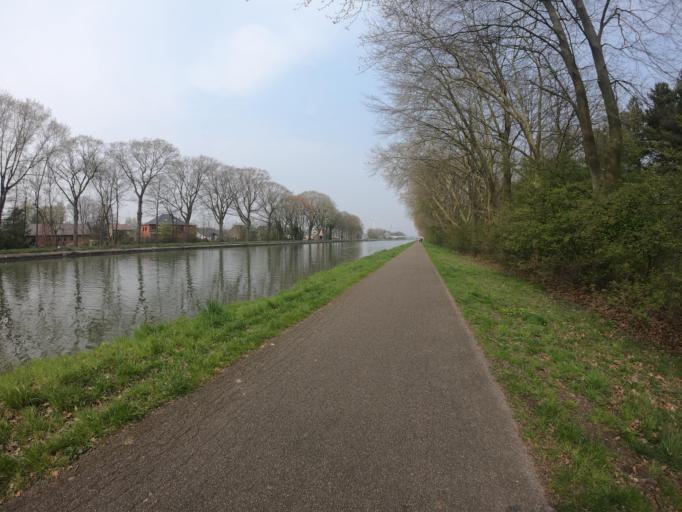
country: BE
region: Flanders
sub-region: Provincie Limburg
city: Maasmechelen
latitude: 51.0338
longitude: 5.7059
